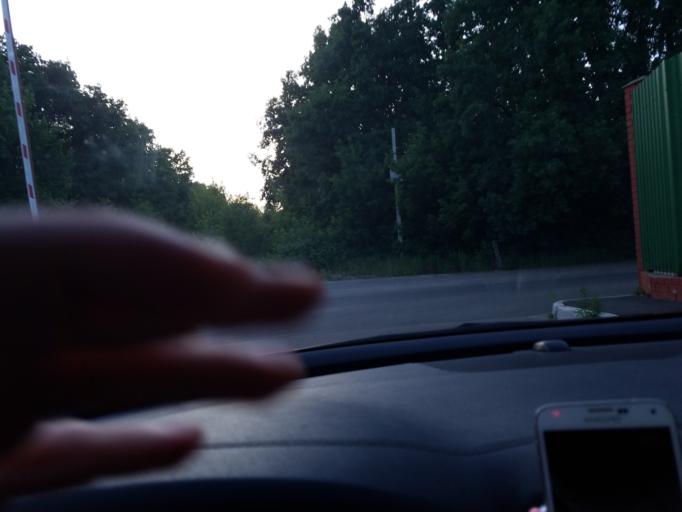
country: RU
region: Orjol
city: Znamenka
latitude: 52.9125
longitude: 36.0060
